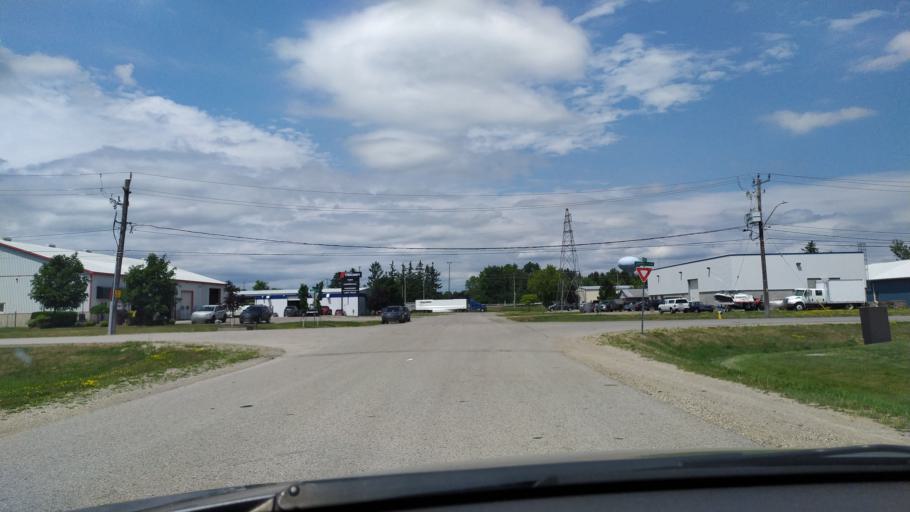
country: CA
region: Ontario
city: Stratford
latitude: 43.3514
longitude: -80.9900
